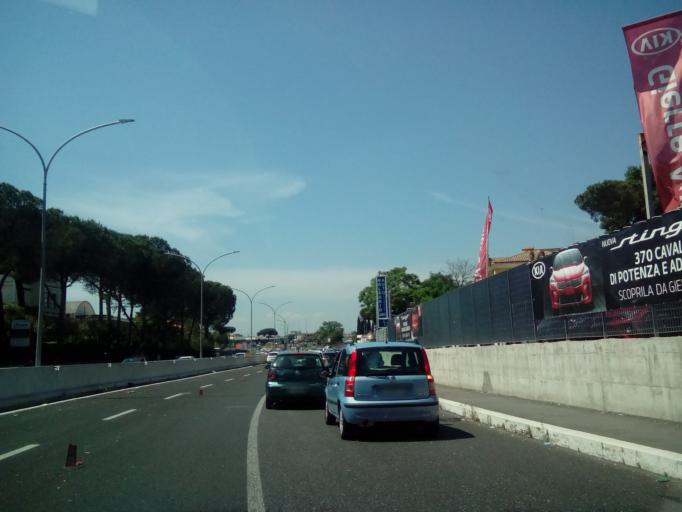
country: IT
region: Latium
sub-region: Citta metropolitana di Roma Capitale
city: Colle Verde
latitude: 41.9290
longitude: 12.5769
